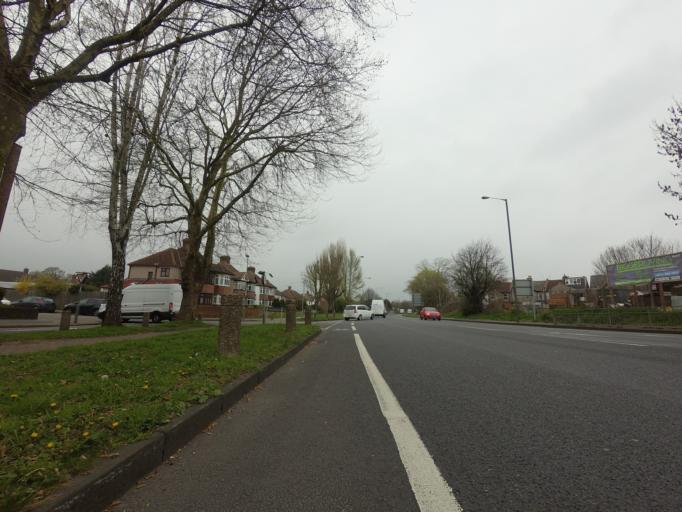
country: GB
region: England
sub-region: Greater London
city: Orpington
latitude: 51.3831
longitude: 0.1074
